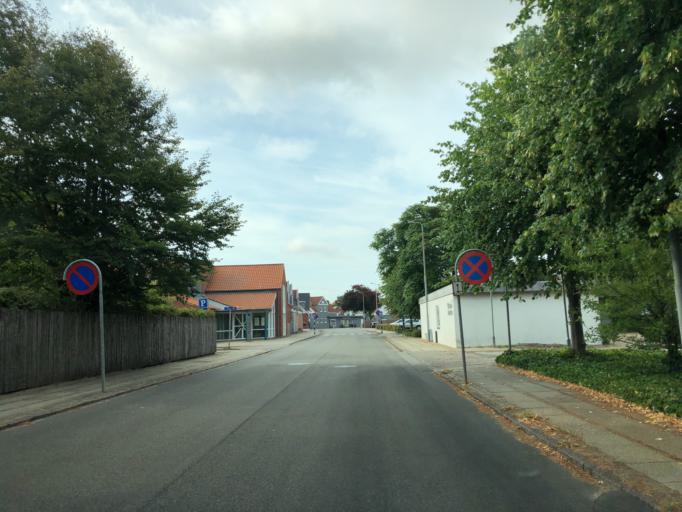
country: DK
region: Central Jutland
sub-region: Ringkobing-Skjern Kommune
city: Skjern
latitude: 55.9471
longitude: 8.4956
